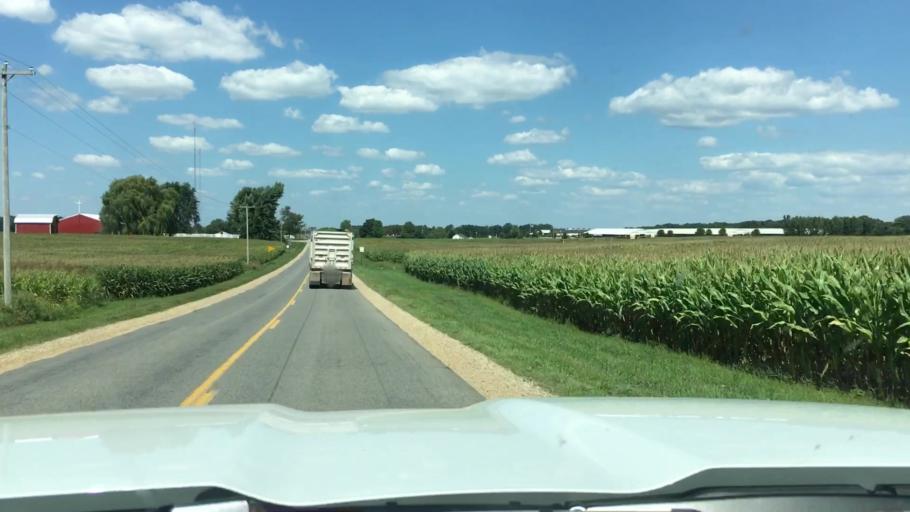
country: US
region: Michigan
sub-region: Muskegon County
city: Ravenna
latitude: 43.2865
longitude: -85.9080
